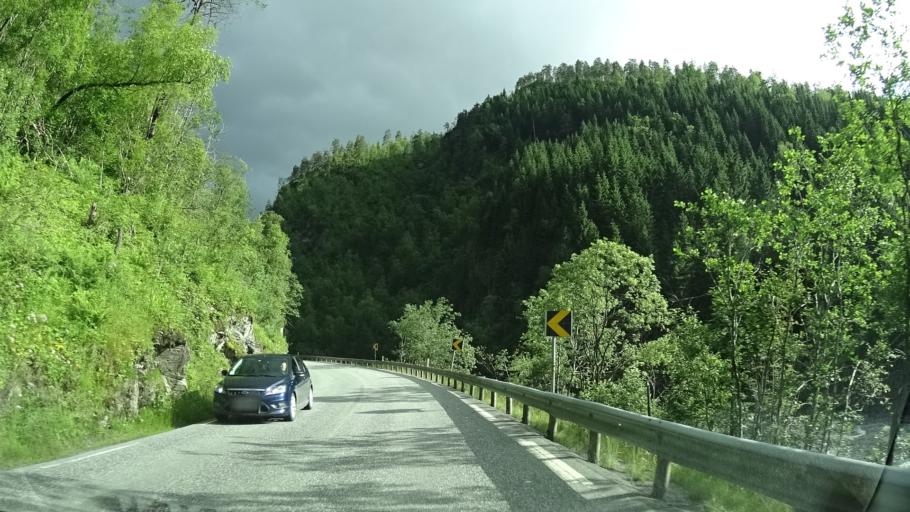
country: NO
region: Hordaland
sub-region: Voss
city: Voss
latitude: 60.7601
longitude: 6.4908
